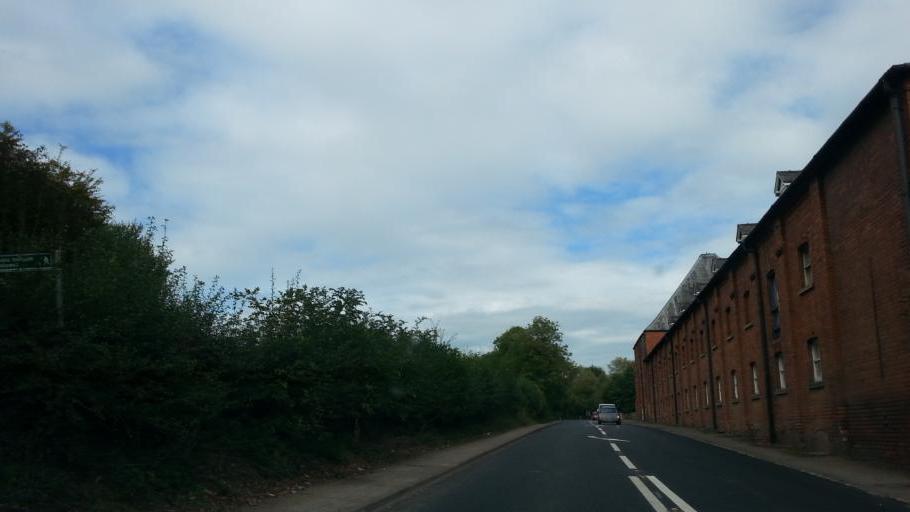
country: GB
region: England
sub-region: Gloucestershire
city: Stroud
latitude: 51.7527
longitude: -2.2227
